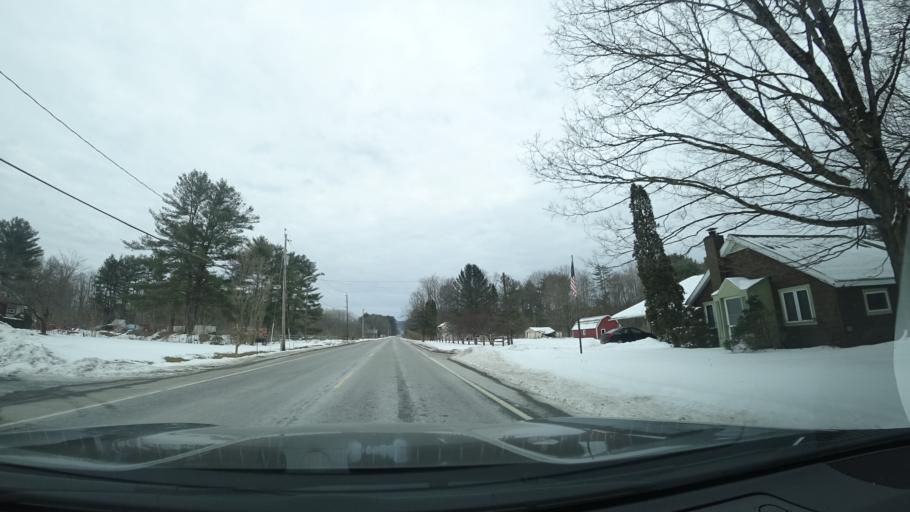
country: US
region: New York
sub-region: Washington County
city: Cambridge
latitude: 43.1503
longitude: -73.3685
